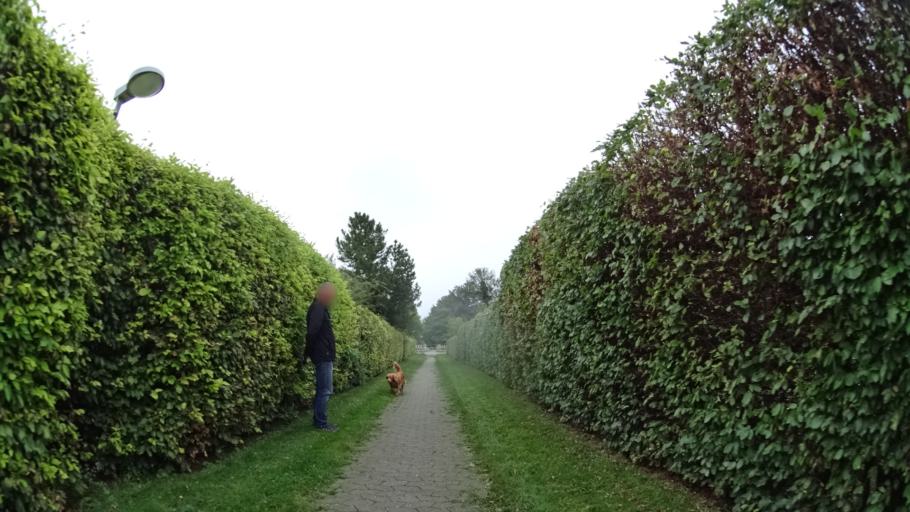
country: DK
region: Central Jutland
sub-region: Arhus Kommune
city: Arhus
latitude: 56.1641
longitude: 10.1597
